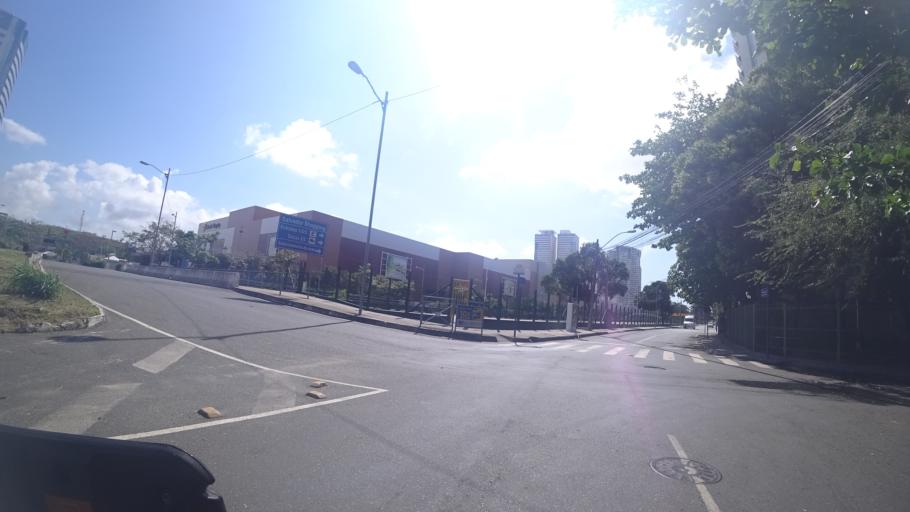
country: BR
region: Bahia
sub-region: Salvador
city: Salvador
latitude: -12.9783
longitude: -38.4576
